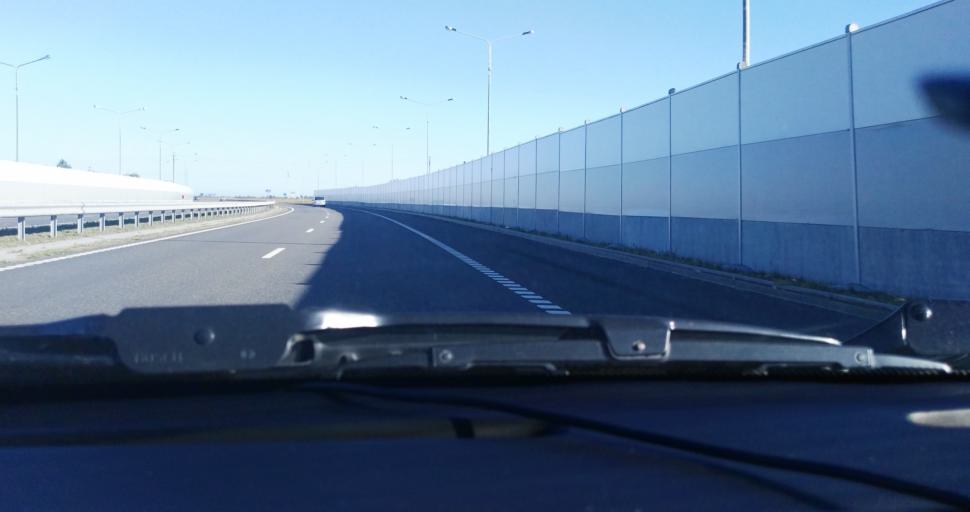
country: BY
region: Gomel
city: Buda-Kashalyova
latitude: 52.5182
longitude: 30.6277
